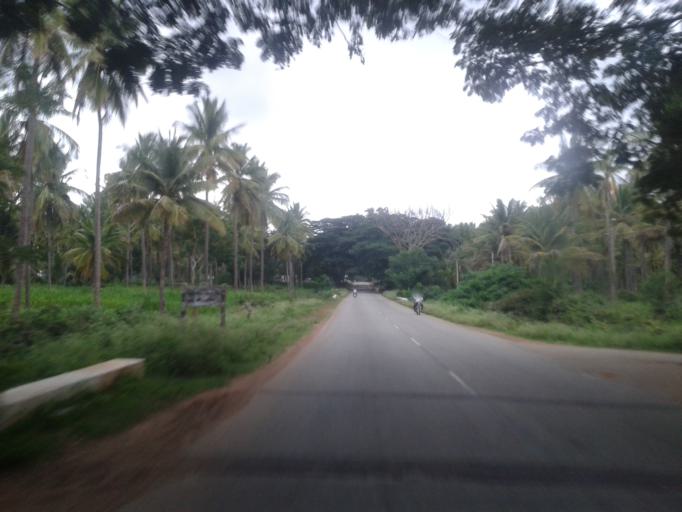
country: IN
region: Karnataka
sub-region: Hassan
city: Shravanabelagola
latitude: 12.8743
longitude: 76.4419
